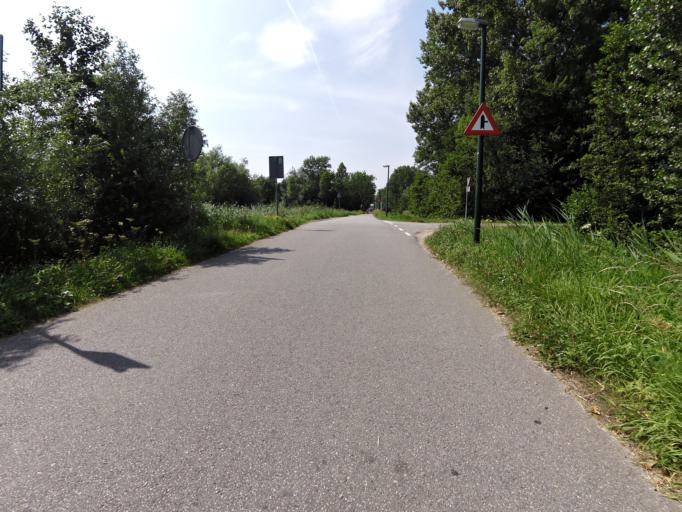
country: NL
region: South Holland
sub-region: Gemeente Dordrecht
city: Dordrecht
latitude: 51.7769
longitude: 4.6584
